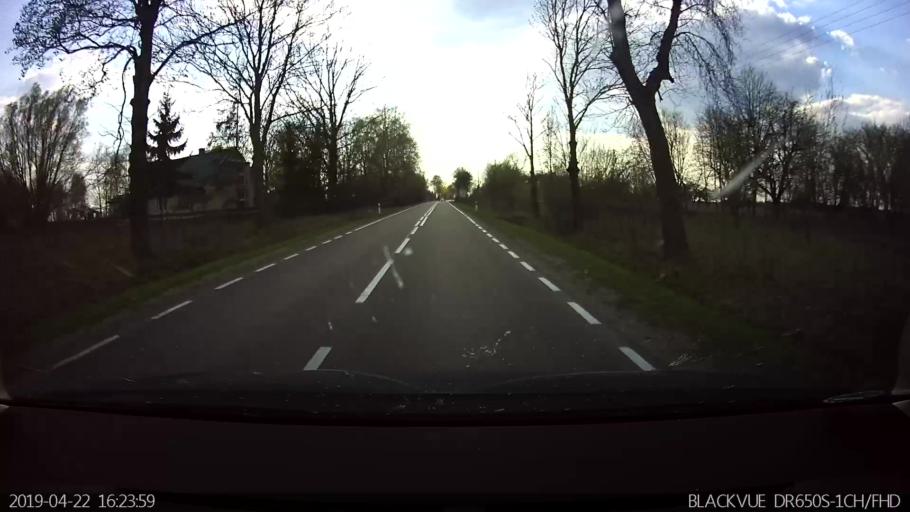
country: PL
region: Podlasie
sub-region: Powiat hajnowski
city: Kleszczele
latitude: 52.5566
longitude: 23.2742
